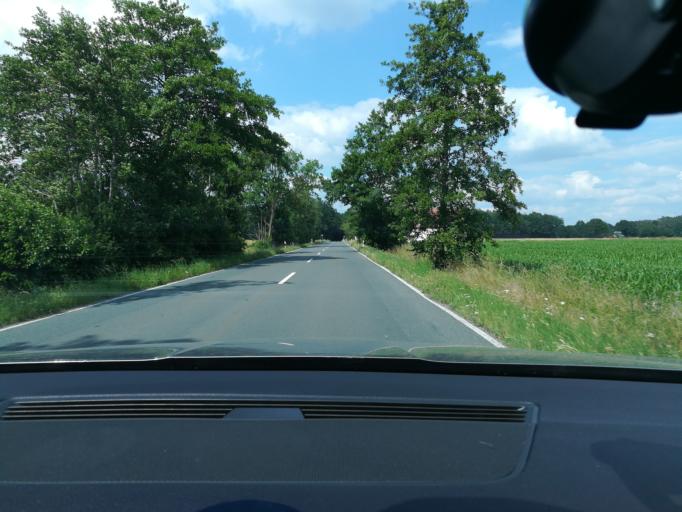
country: DE
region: North Rhine-Westphalia
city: Espelkamp
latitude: 52.3663
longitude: 8.6806
